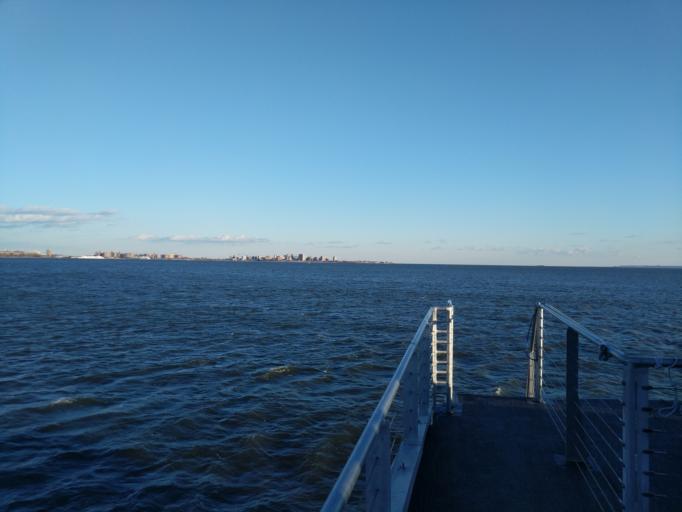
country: US
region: New York
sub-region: Kings County
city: Bensonhurst
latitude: 40.6059
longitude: -74.0386
